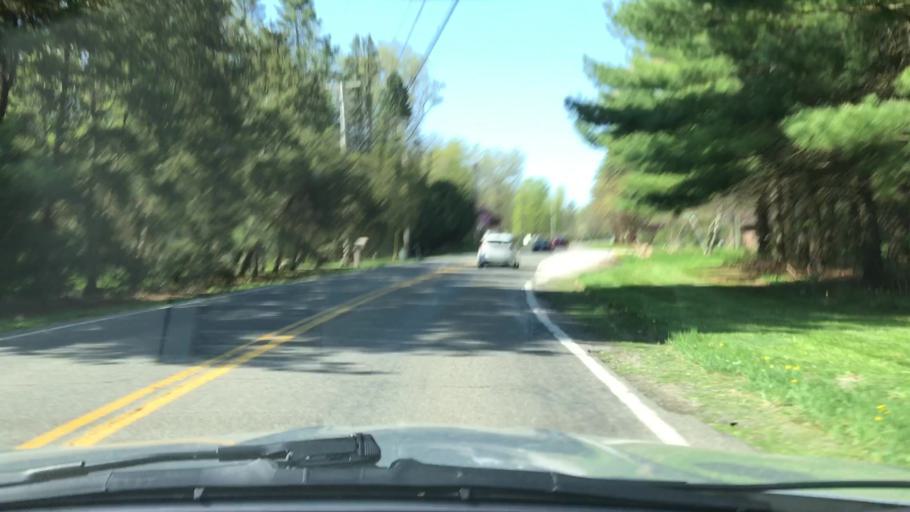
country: US
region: Indiana
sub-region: Saint Joseph County
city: Georgetown
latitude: 41.7577
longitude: -86.3037
